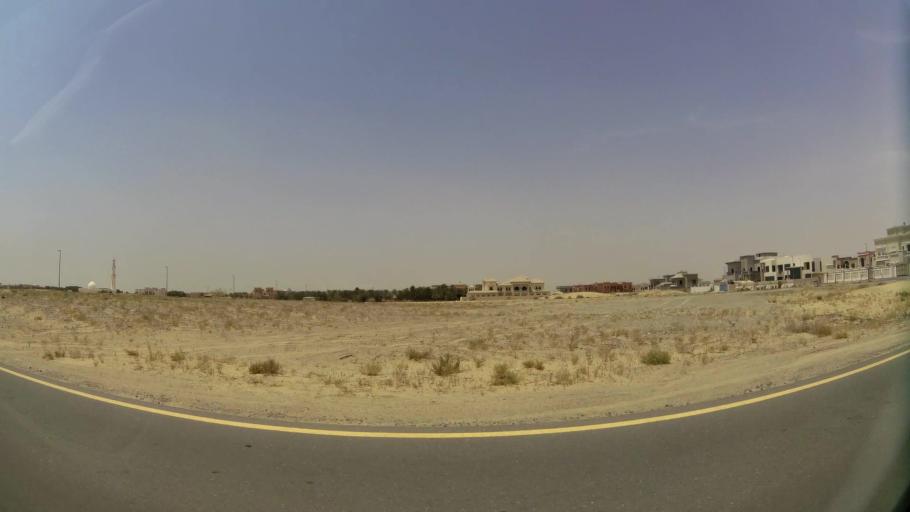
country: AE
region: Ash Shariqah
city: Sharjah
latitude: 25.2377
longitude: 55.4854
